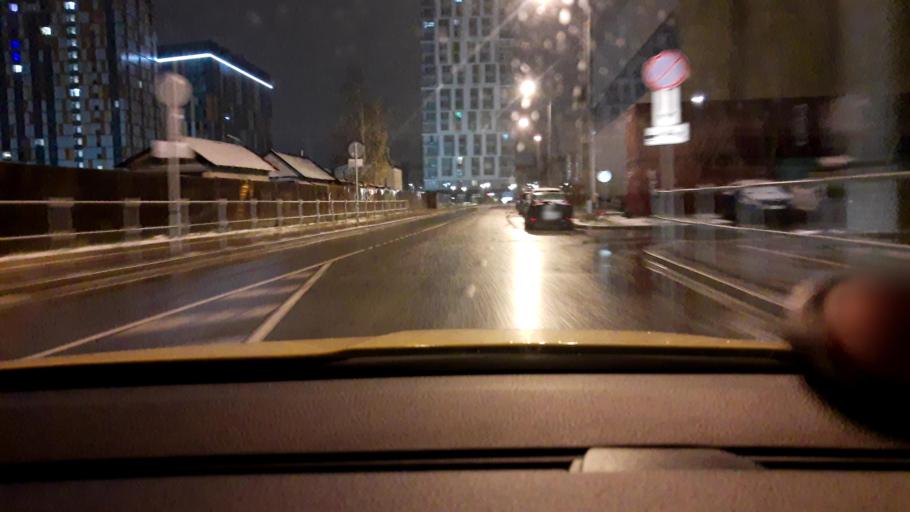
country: RU
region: Moskovskaya
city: Pavshino
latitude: 55.8445
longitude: 37.3736
